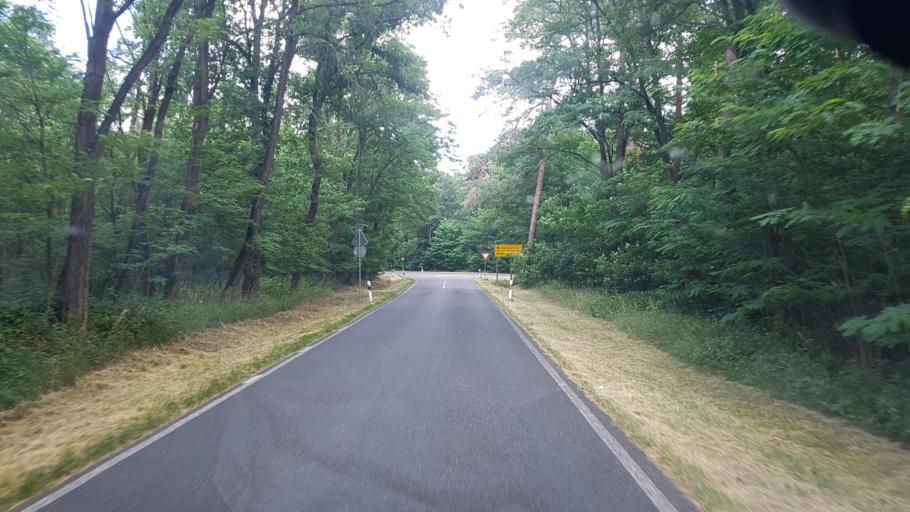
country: DE
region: Brandenburg
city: Sallgast
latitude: 51.5863
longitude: 13.9208
